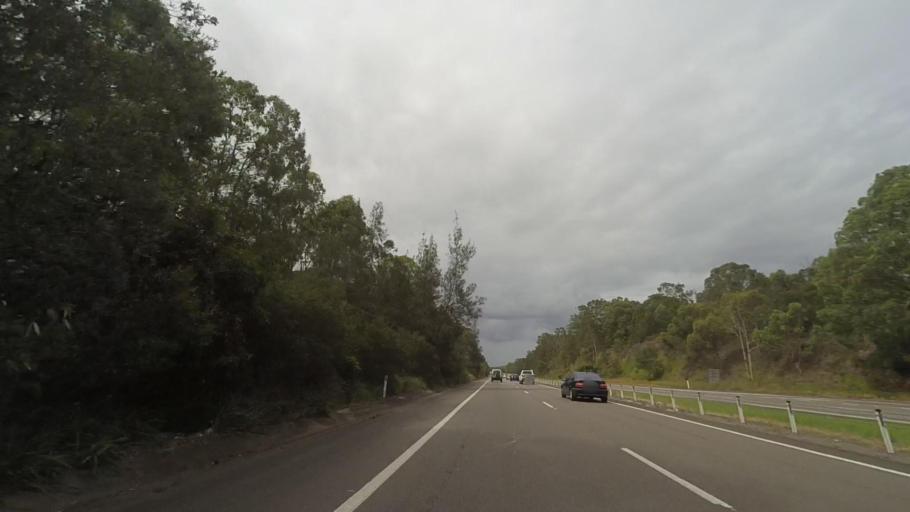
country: AU
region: New South Wales
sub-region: Port Stephens Shire
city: Raymond Terrace
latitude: -32.7391
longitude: 151.7780
